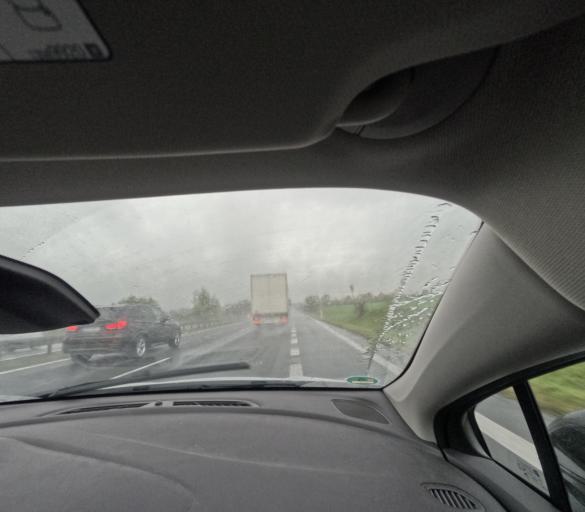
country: CZ
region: Central Bohemia
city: Velka Dobra
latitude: 50.1050
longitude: 14.0832
